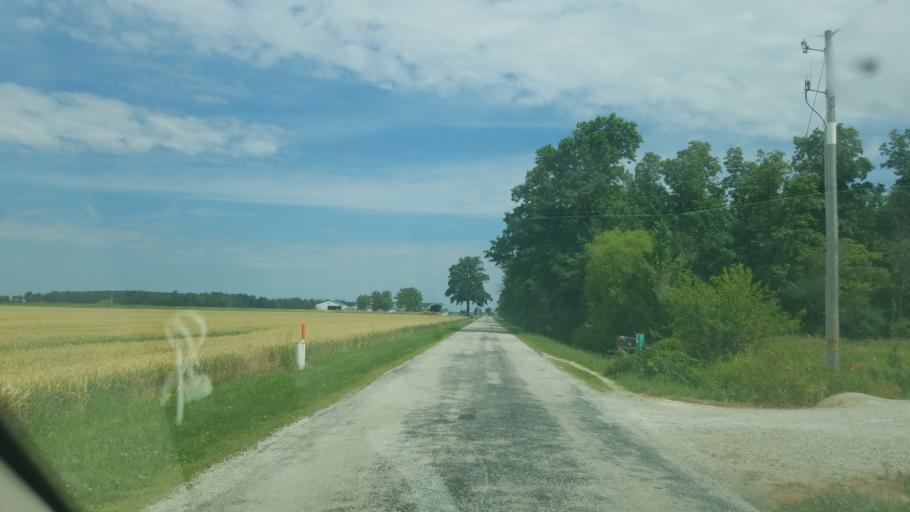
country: US
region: Ohio
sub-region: Wood County
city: North Baltimore
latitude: 41.2063
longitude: -83.5733
